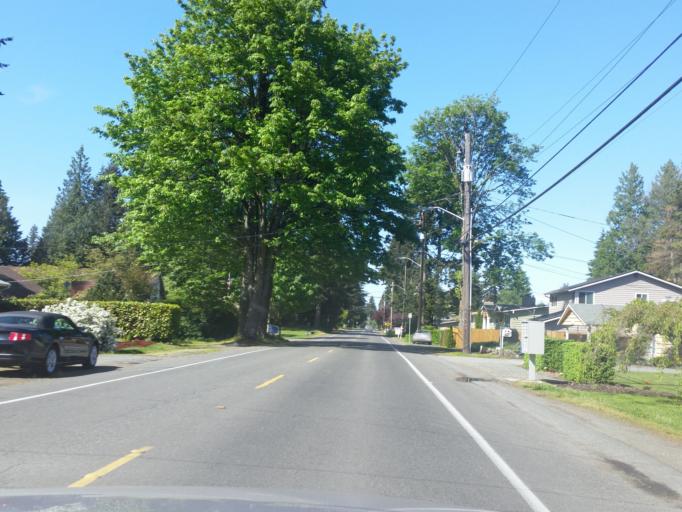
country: US
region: Washington
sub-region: King County
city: Shoreline
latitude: 47.7711
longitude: -122.3513
